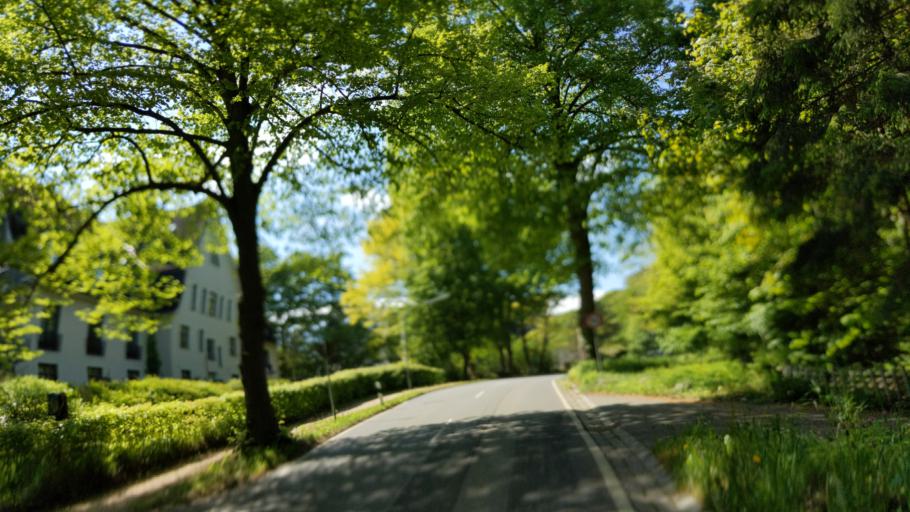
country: DE
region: Schleswig-Holstein
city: Malente
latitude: 54.1851
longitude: 10.5953
